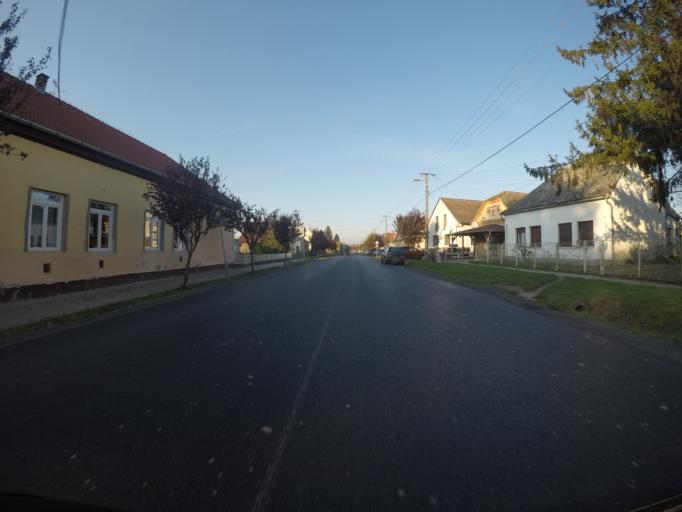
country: HU
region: Somogy
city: Barcs
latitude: 45.9810
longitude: 17.5897
